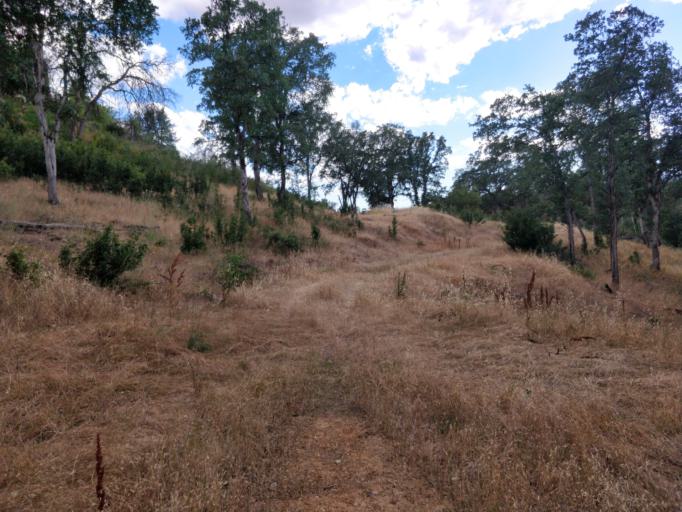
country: US
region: California
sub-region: Shasta County
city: Redding
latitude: 40.6116
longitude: -122.3853
